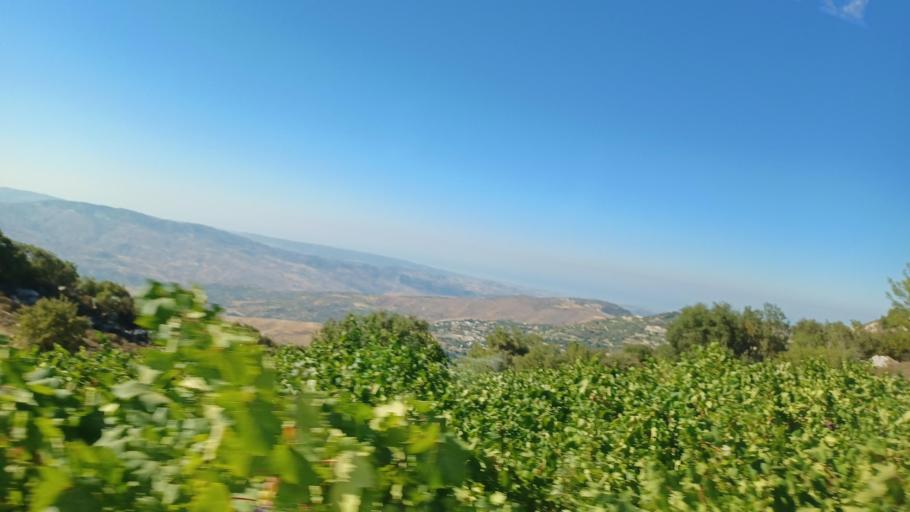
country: CY
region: Limassol
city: Pachna
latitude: 34.8988
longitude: 32.6368
